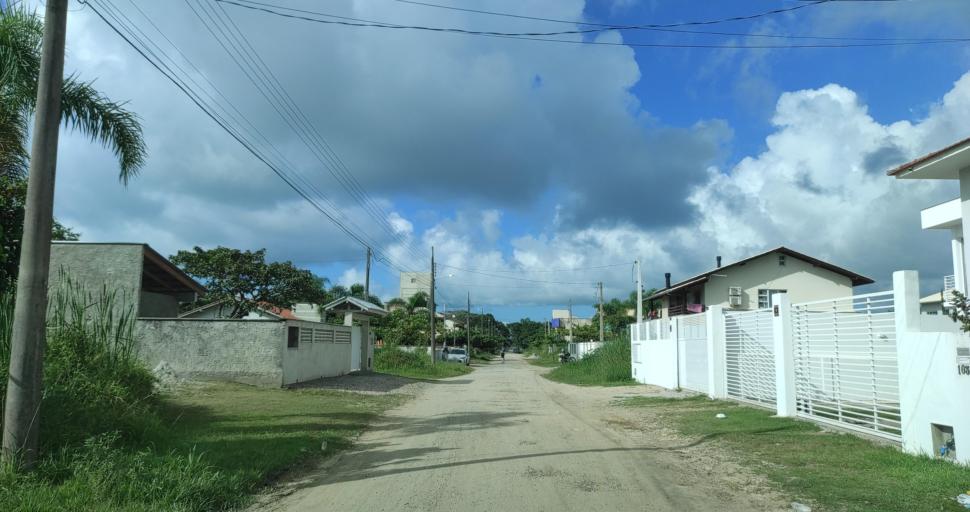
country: BR
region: Santa Catarina
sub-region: Porto Belo
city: Porto Belo
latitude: -27.1774
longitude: -48.5059
